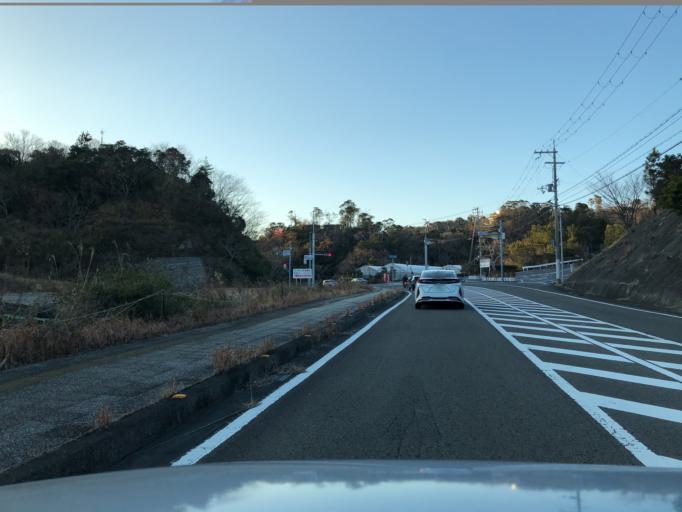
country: JP
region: Wakayama
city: Tanabe
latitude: 33.6624
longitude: 135.3743
